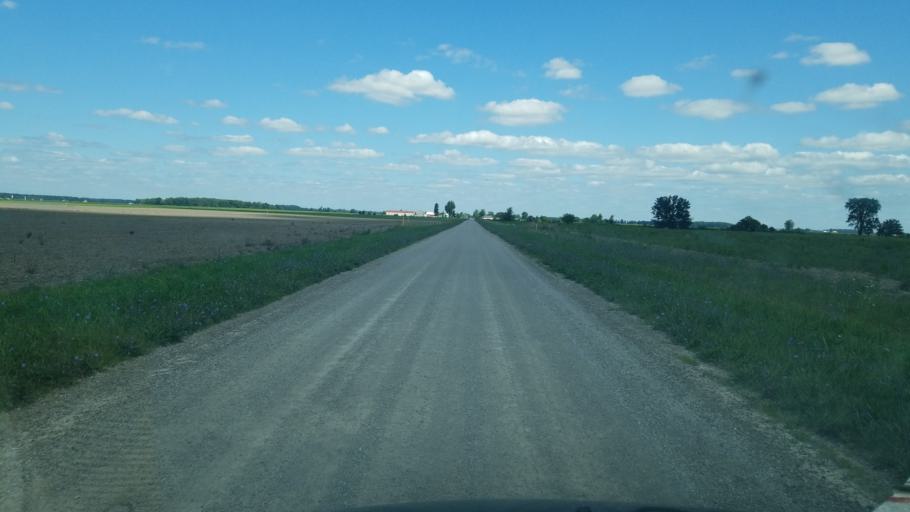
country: US
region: Ohio
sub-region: Fulton County
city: Delta
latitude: 41.7187
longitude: -84.0180
